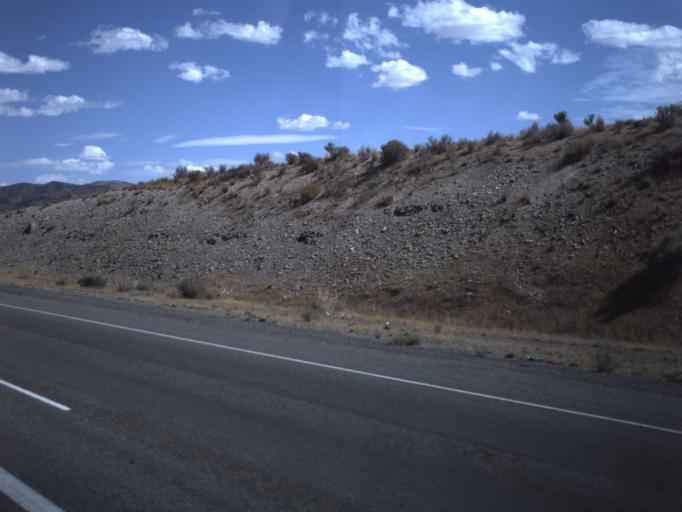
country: US
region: Utah
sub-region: Tooele County
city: Grantsville
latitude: 40.7597
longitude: -113.0109
